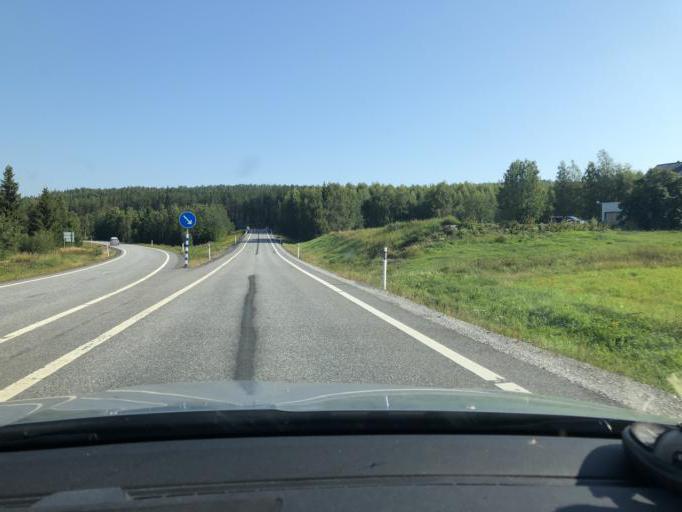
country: SE
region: Vaesternorrland
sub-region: Kramfors Kommun
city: Nordingra
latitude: 62.9332
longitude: 18.0909
